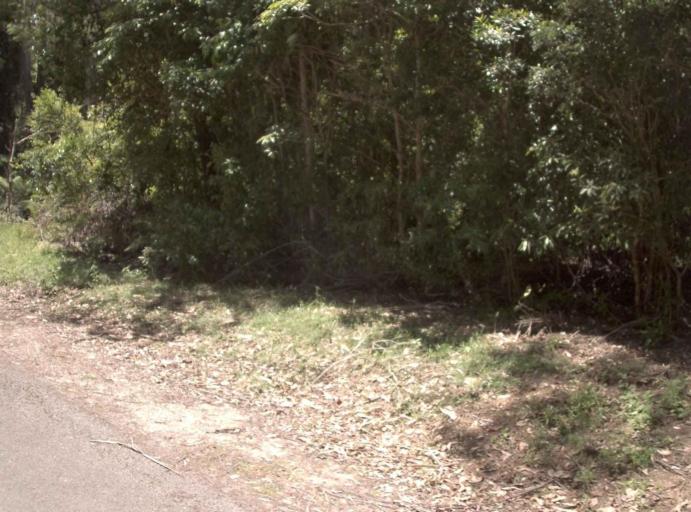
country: AU
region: New South Wales
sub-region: Bombala
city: Bombala
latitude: -37.4929
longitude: 148.9254
